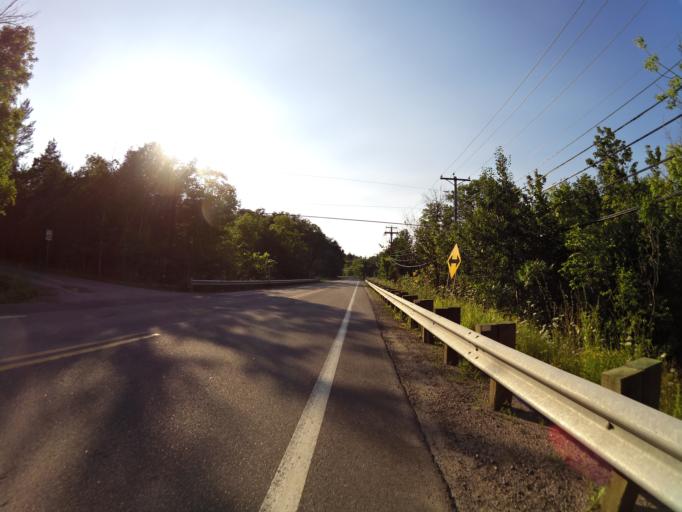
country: CA
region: Quebec
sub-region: Outaouais
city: Wakefield
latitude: 45.5700
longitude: -75.8606
